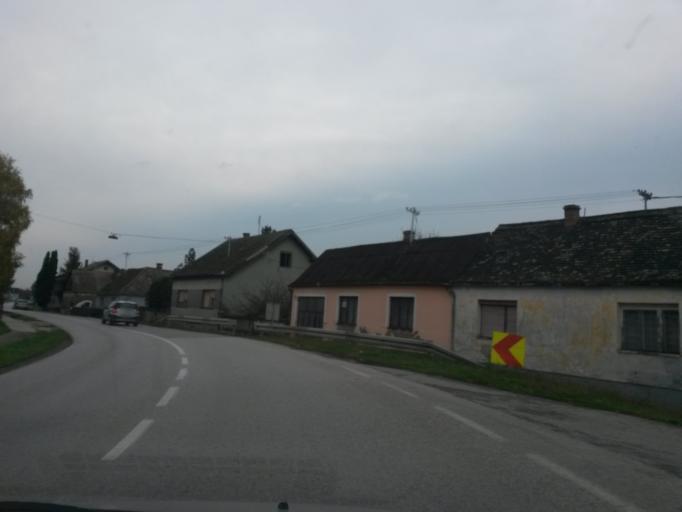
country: HR
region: Osjecko-Baranjska
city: Darda
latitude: 45.6241
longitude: 18.6914
